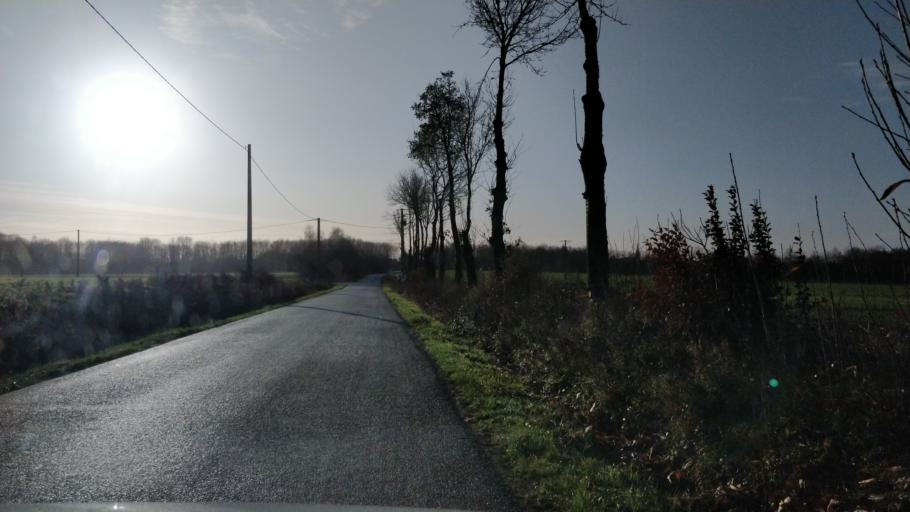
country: FR
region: Brittany
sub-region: Departement d'Ille-et-Vilaine
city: Chavagne
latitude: 48.0624
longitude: -1.7896
